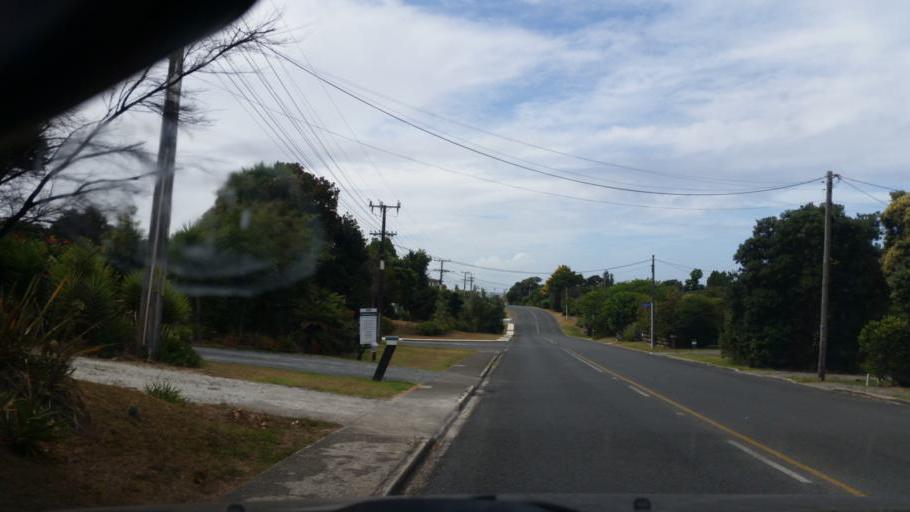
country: NZ
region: Auckland
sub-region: Auckland
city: Wellsford
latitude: -36.0868
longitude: 174.5840
